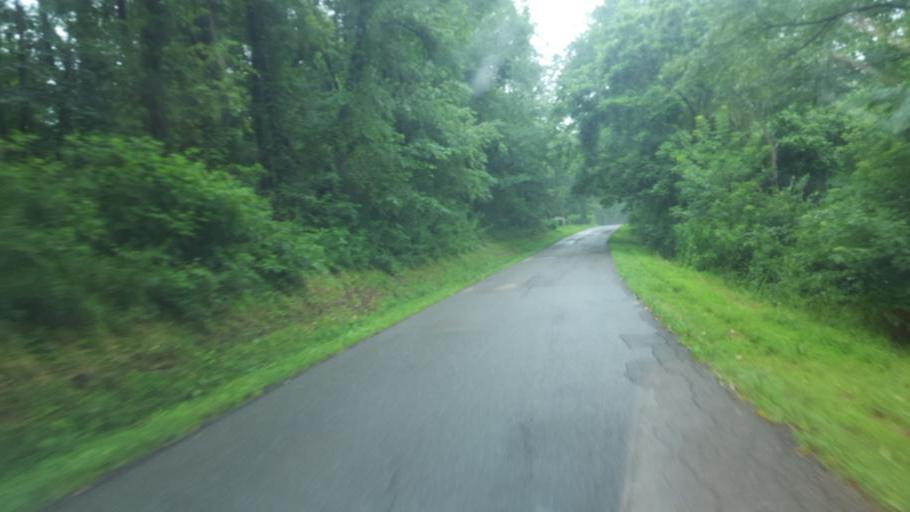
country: US
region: Ohio
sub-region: Columbiana County
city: Salineville
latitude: 40.5583
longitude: -80.8430
